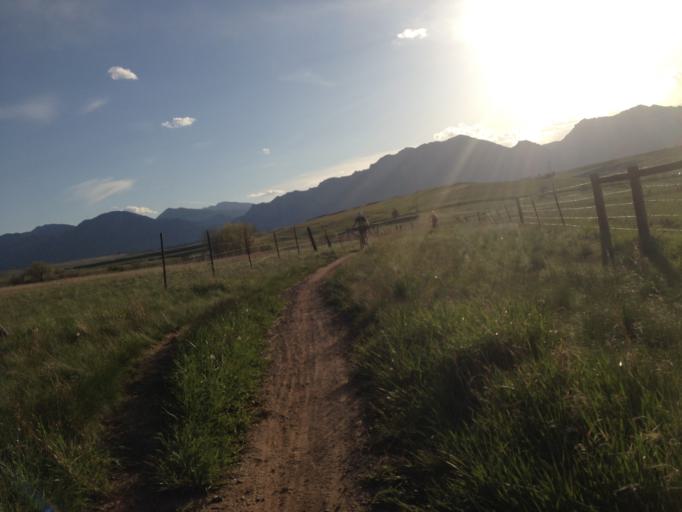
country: US
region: Colorado
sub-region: Boulder County
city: Superior
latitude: 39.9576
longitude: -105.1929
